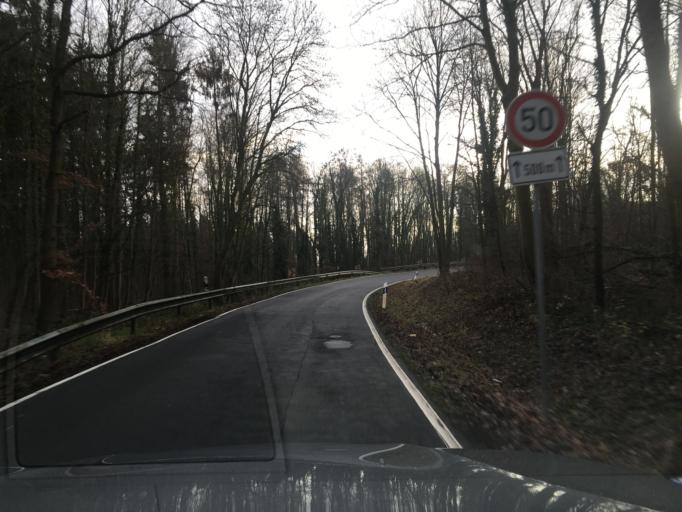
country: DE
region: Rheinland-Pfalz
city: Remagen
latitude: 50.5810
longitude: 7.2142
